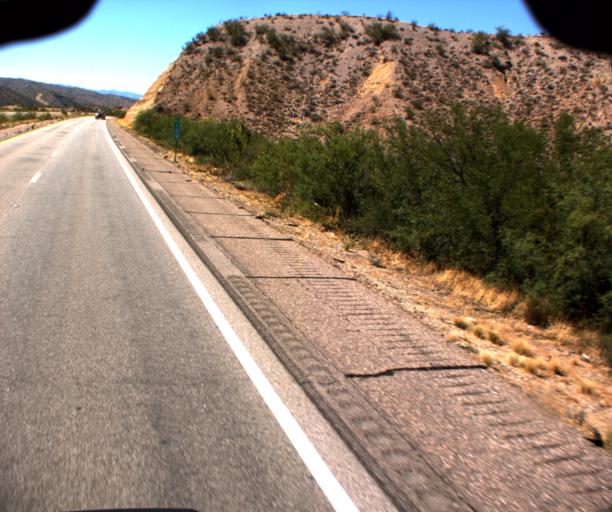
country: US
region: Arizona
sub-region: Yavapai County
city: Bagdad
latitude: 34.6401
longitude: -113.5618
